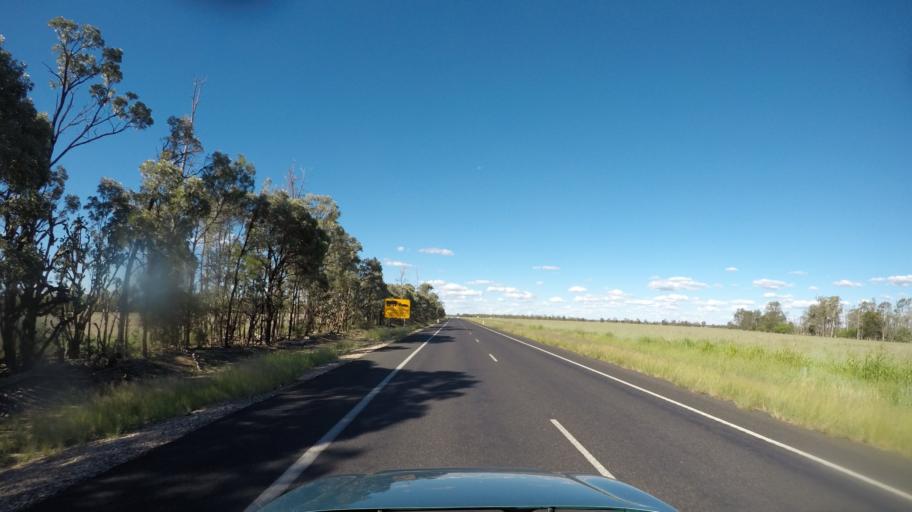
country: AU
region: Queensland
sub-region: Goondiwindi
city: Goondiwindi
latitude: -28.1309
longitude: 150.6997
